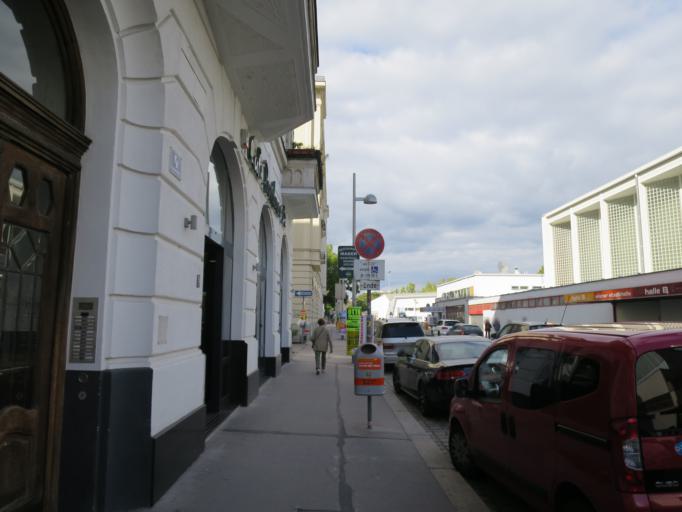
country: AT
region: Vienna
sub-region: Wien Stadt
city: Vienna
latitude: 48.2015
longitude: 16.3315
